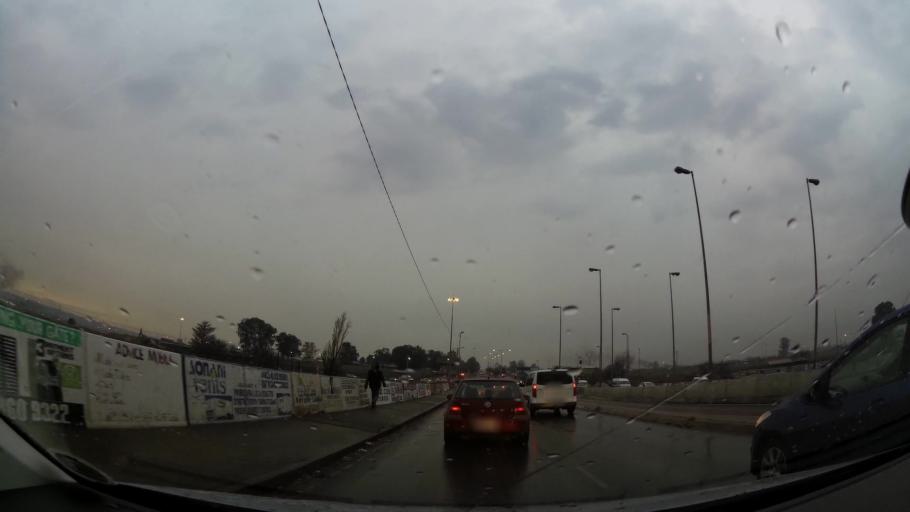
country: ZA
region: Gauteng
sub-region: City of Johannesburg Metropolitan Municipality
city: Soweto
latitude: -26.2626
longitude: 27.8887
